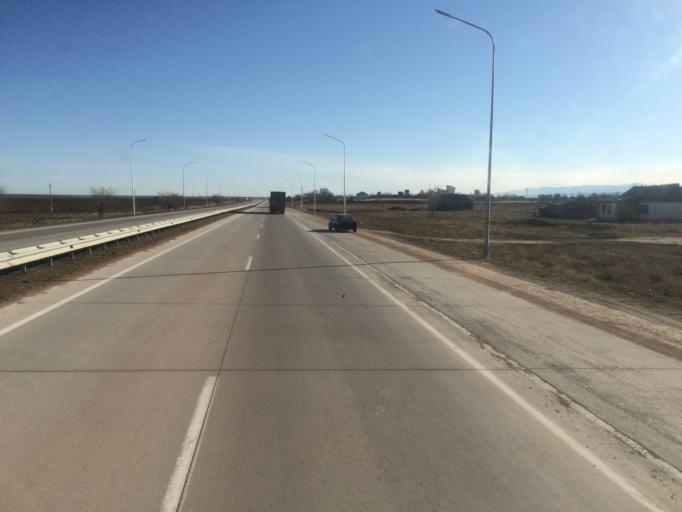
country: KZ
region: Zhambyl
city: Kulan
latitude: 42.9929
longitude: 72.3108
